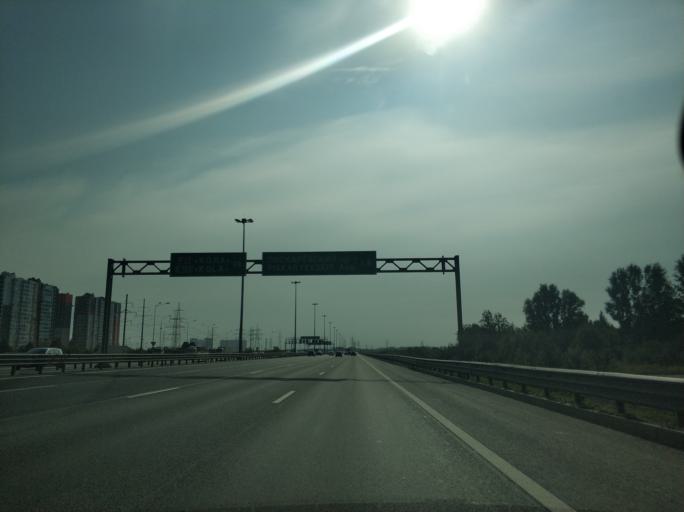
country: RU
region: Leningrad
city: Murino
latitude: 60.0291
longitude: 30.4462
